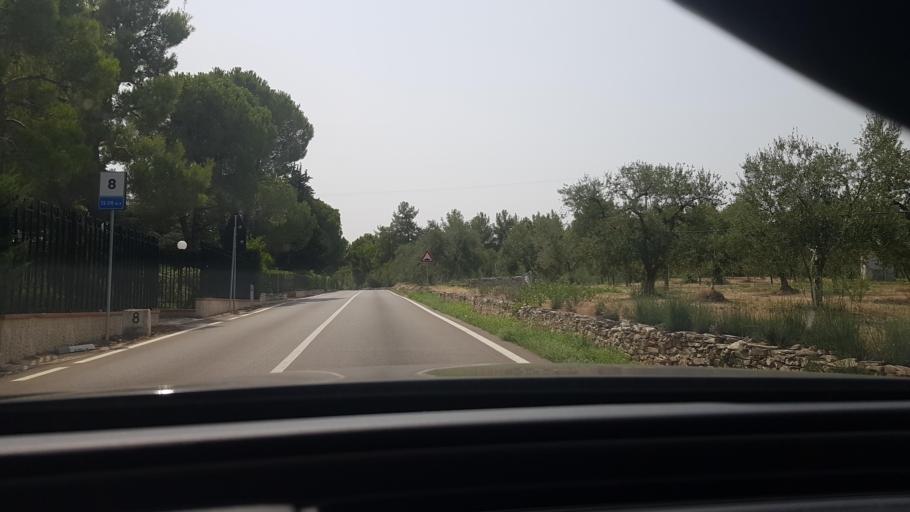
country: IT
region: Apulia
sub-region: Provincia di Barletta - Andria - Trani
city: Andria
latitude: 41.1428
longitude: 16.2895
